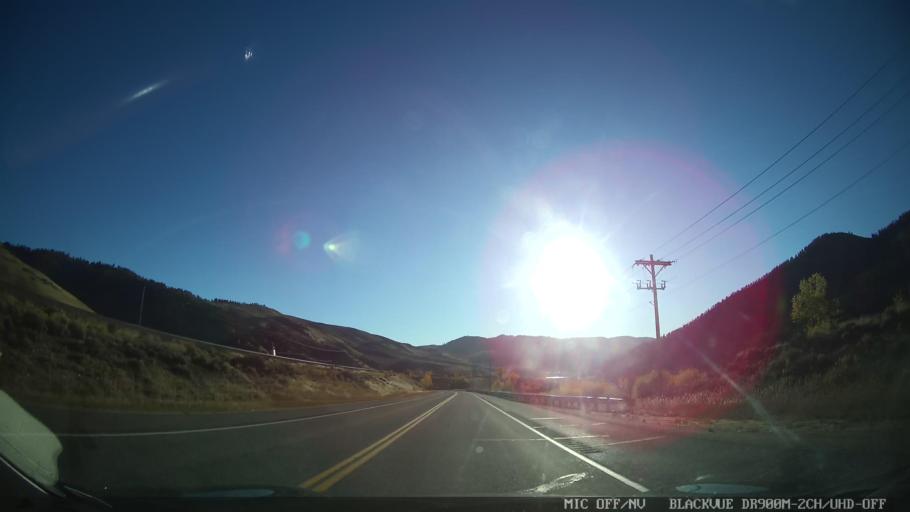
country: US
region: Colorado
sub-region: Grand County
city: Hot Sulphur Springs
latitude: 40.0507
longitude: -106.1393
